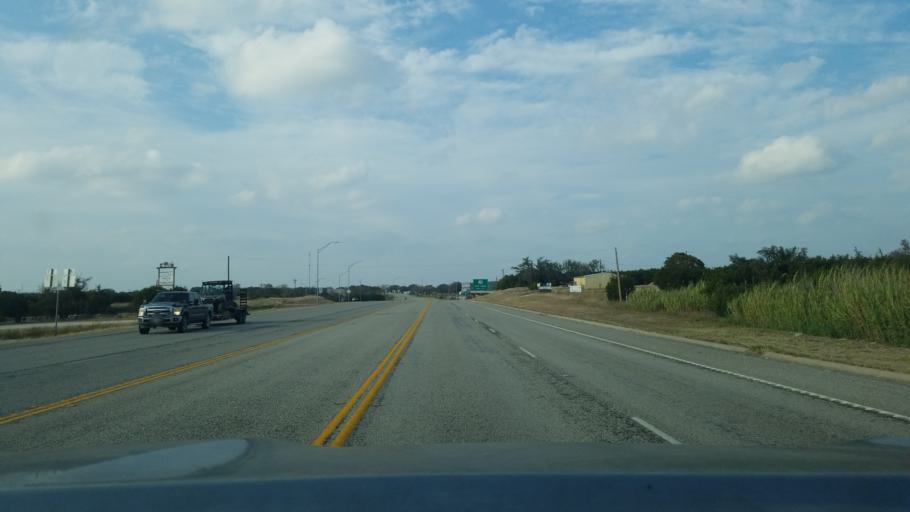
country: US
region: Texas
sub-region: Lampasas County
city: Lampasas
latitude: 31.2045
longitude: -98.3877
